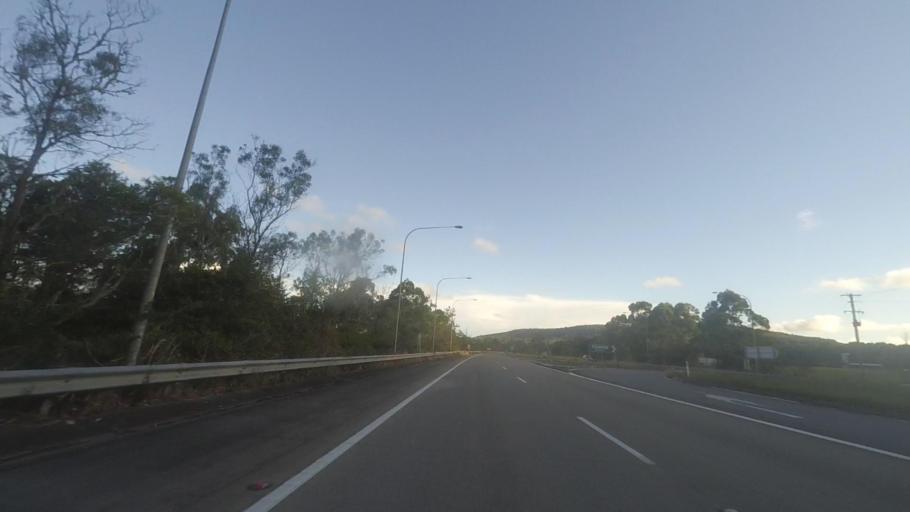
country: AU
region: New South Wales
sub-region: Great Lakes
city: Nabiac
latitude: -32.2606
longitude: 152.3268
